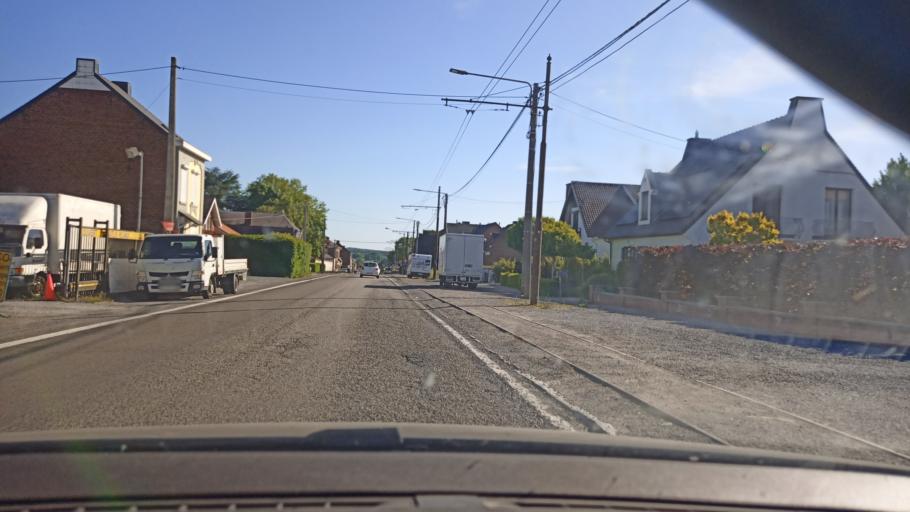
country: BE
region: Wallonia
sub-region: Province du Hainaut
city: Lobbes
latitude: 50.3556
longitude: 4.2690
